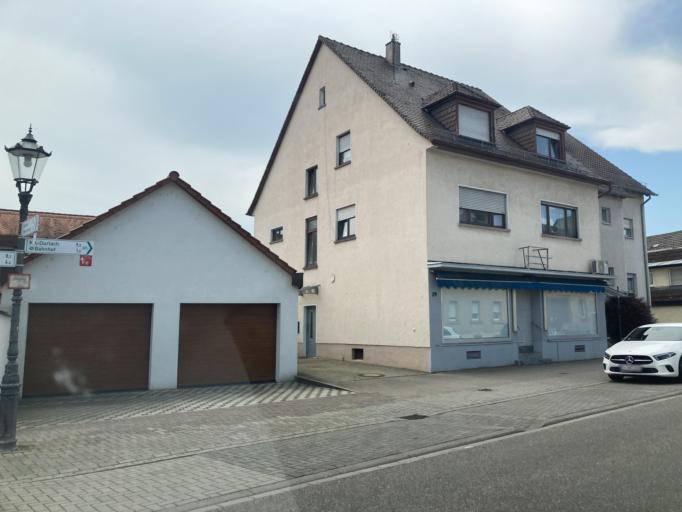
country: DE
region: Baden-Wuerttemberg
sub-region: Karlsruhe Region
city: Weingarten
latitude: 49.0525
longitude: 8.5295
